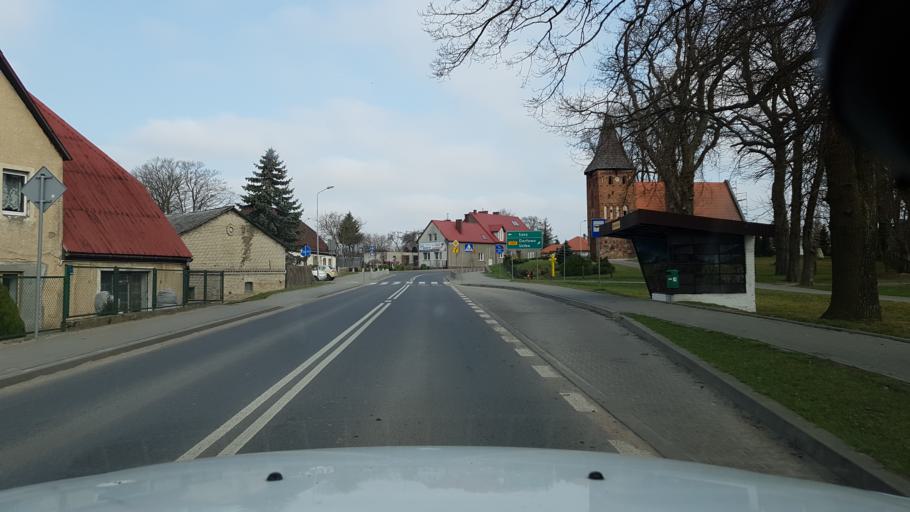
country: PL
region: West Pomeranian Voivodeship
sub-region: Powiat koszalinski
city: Sianow
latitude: 54.2598
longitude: 16.2668
